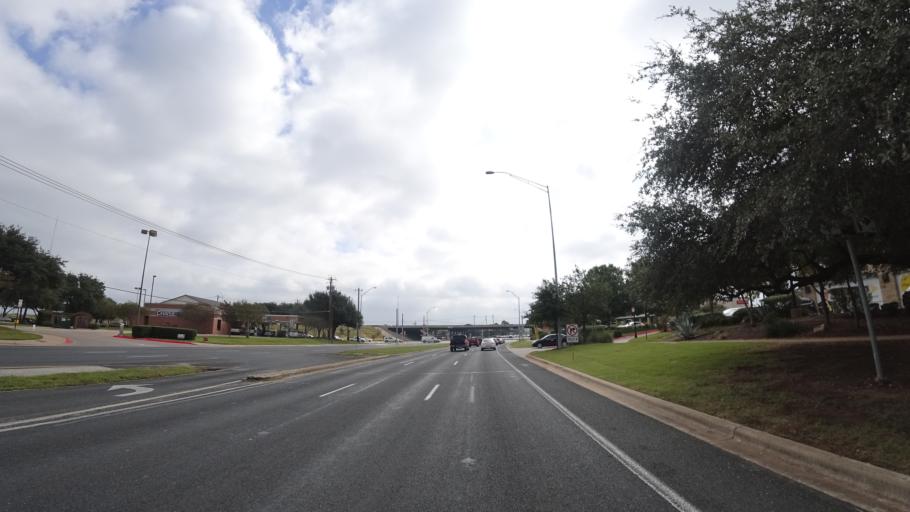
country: US
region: Texas
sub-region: Travis County
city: Shady Hollow
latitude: 30.2216
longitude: -97.8380
